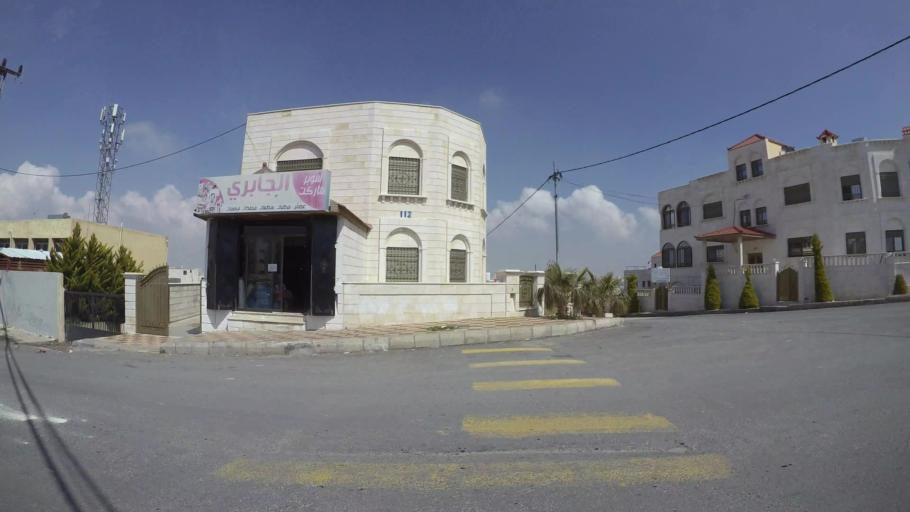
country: JO
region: Amman
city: Al Bunayyat ash Shamaliyah
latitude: 31.8965
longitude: 35.8889
